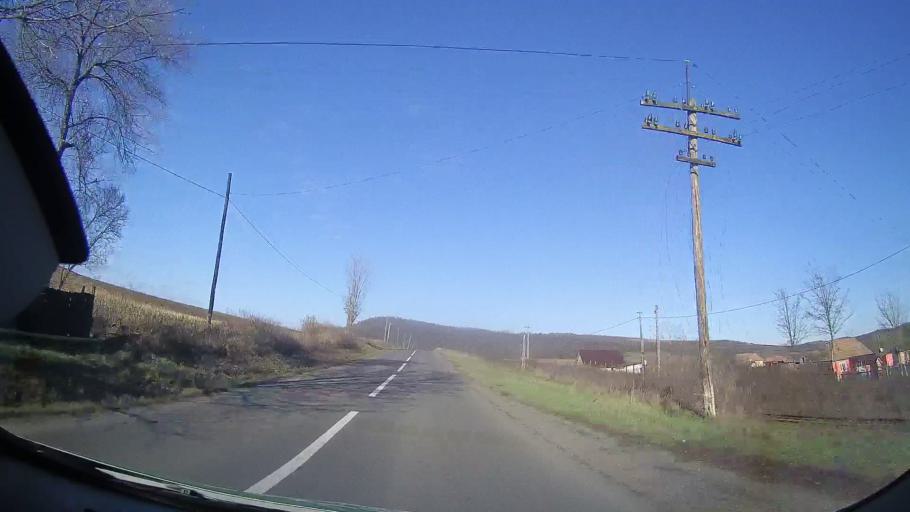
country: RO
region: Mures
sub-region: Comuna Mihesu de Campie
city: Mihesu de Campie
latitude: 46.6639
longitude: 24.1742
